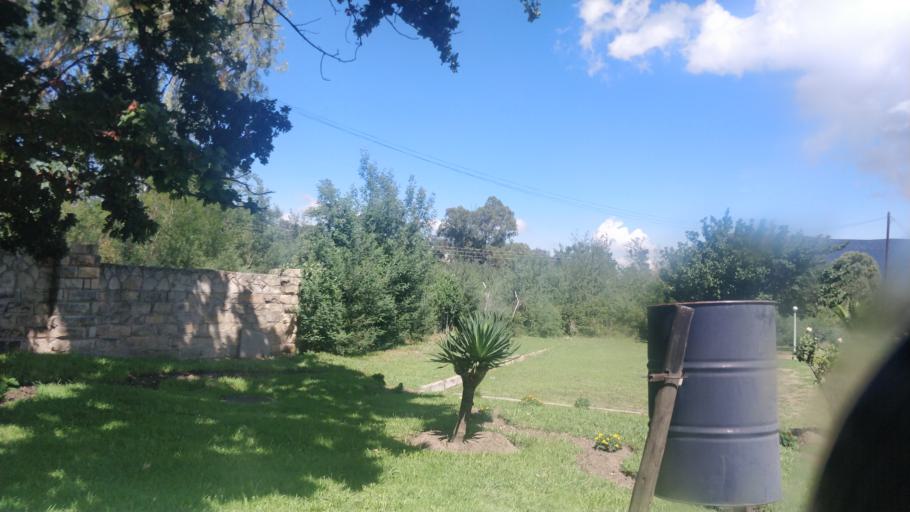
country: LS
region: Maseru
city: Nako
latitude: -29.6285
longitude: 27.5064
